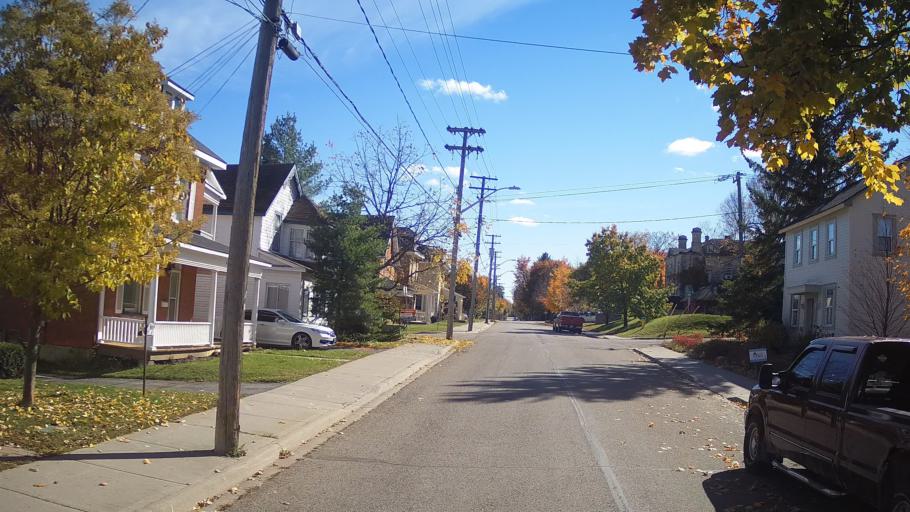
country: CA
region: Ontario
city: Perth
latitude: 44.9000
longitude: -76.2448
